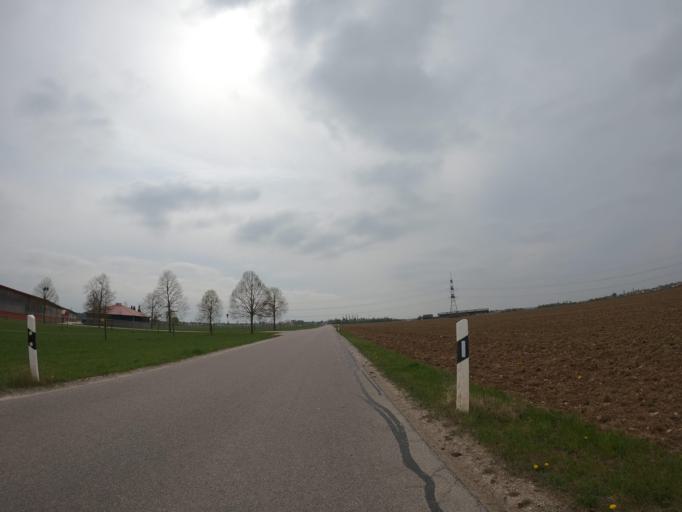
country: DE
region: Bavaria
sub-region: Upper Bavaria
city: Zorneding
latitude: 48.1204
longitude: 11.8083
